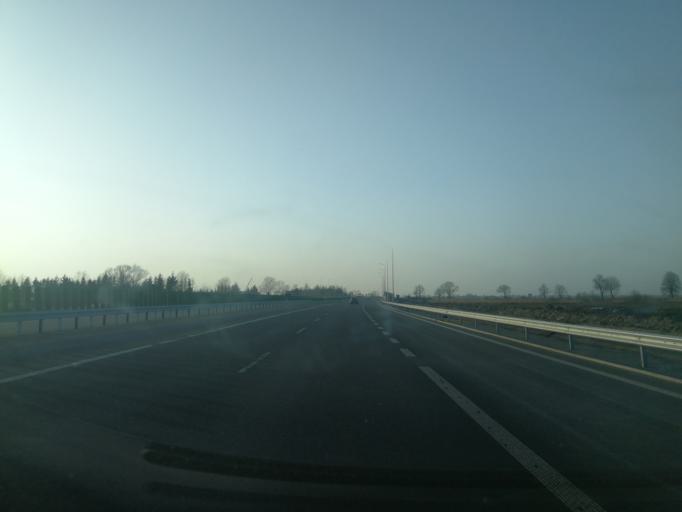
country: PL
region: Pomeranian Voivodeship
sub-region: Powiat nowodworski
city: Nowy Dwor Gdanski
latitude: 54.2241
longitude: 19.0641
